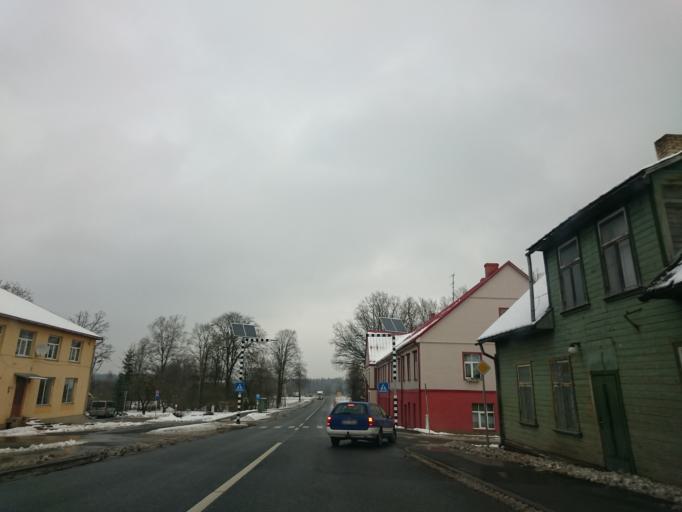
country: LV
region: Pargaujas
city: Stalbe
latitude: 57.3632
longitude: 24.9793
